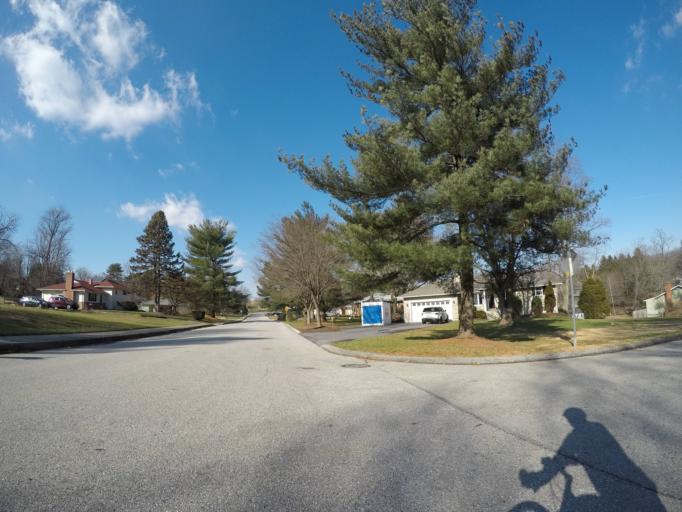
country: US
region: Maryland
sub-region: Howard County
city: Ellicott City
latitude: 39.2384
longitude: -76.7961
